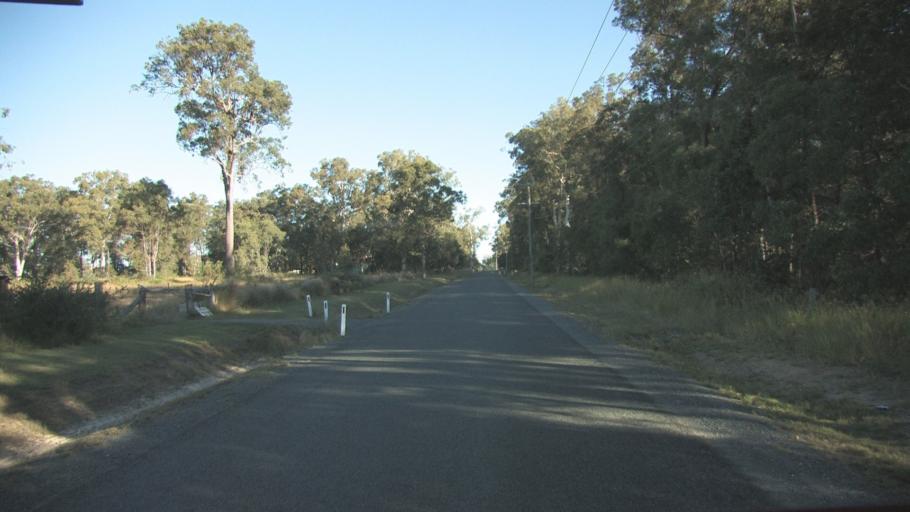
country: AU
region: Queensland
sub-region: Logan
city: Chambers Flat
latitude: -27.7842
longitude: 153.0866
